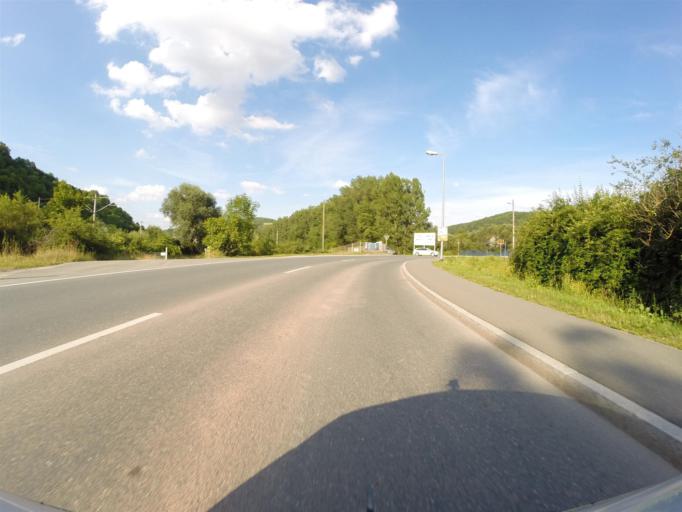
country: DE
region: Thuringia
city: Wichmar
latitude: 51.0090
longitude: 11.6773
